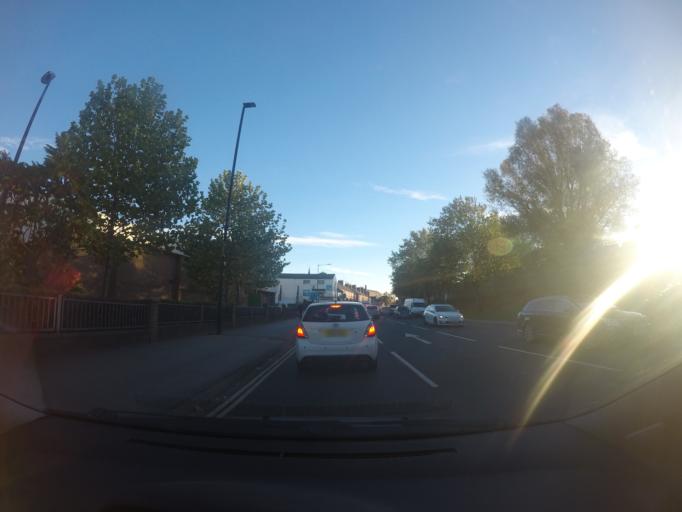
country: GB
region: England
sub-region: City of York
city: York
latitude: 53.9568
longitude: -1.0705
